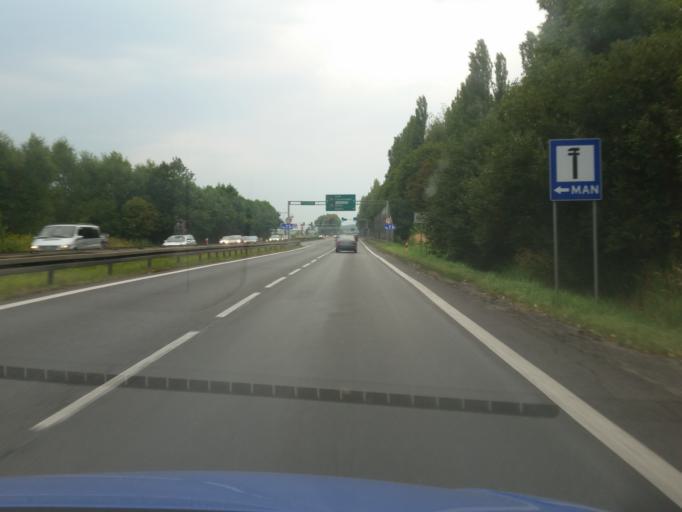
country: PL
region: Silesian Voivodeship
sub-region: Powiat bedzinski
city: Bedzin
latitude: 50.3113
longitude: 19.1114
